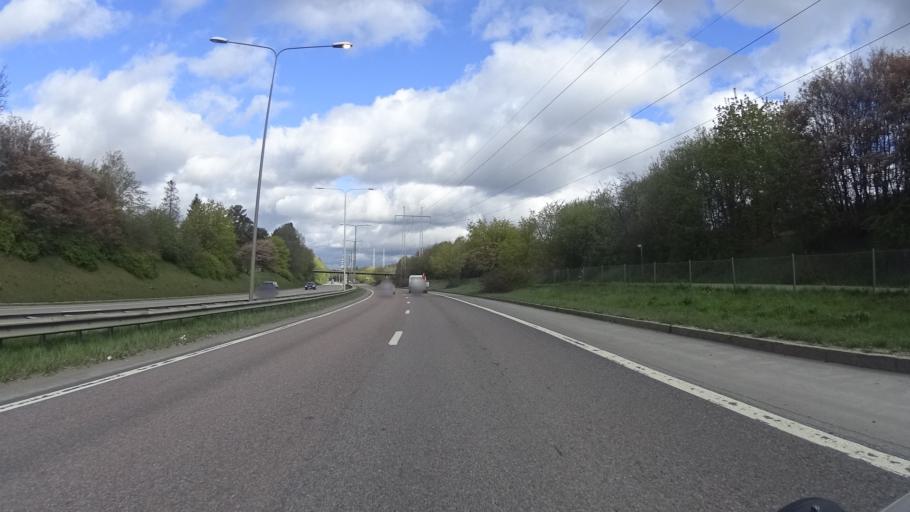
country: SE
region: Stockholm
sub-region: Stockholms Kommun
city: Arsta
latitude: 59.2651
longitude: 18.0624
